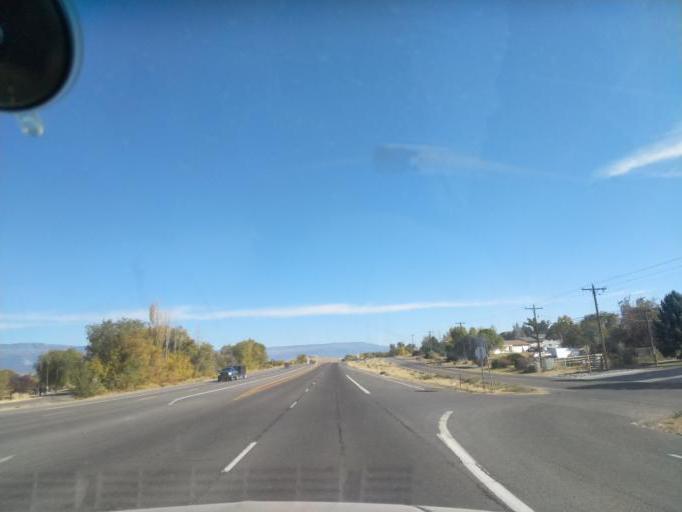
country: US
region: Colorado
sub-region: Mesa County
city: Orchard Mesa
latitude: 39.0267
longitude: -108.5066
